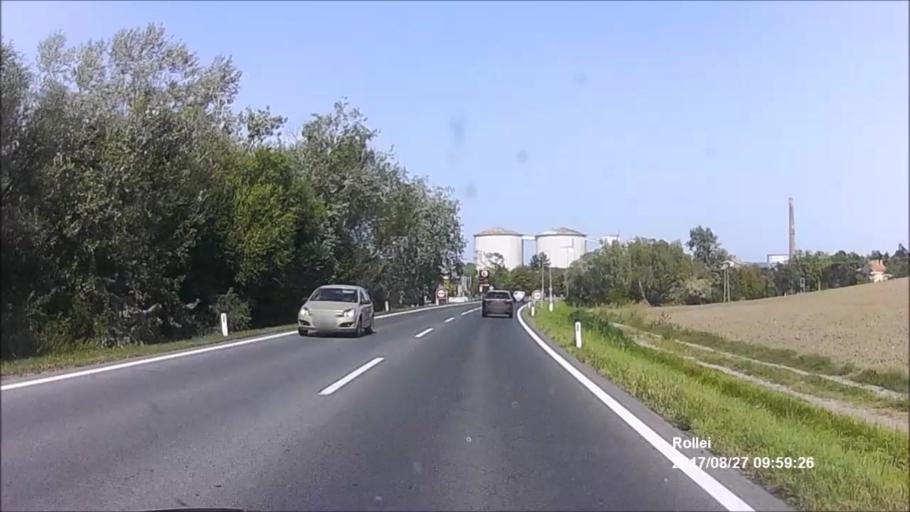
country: AT
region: Burgenland
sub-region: Eisenstadt-Umgebung
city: Klingenbach
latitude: 47.7654
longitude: 16.5344
